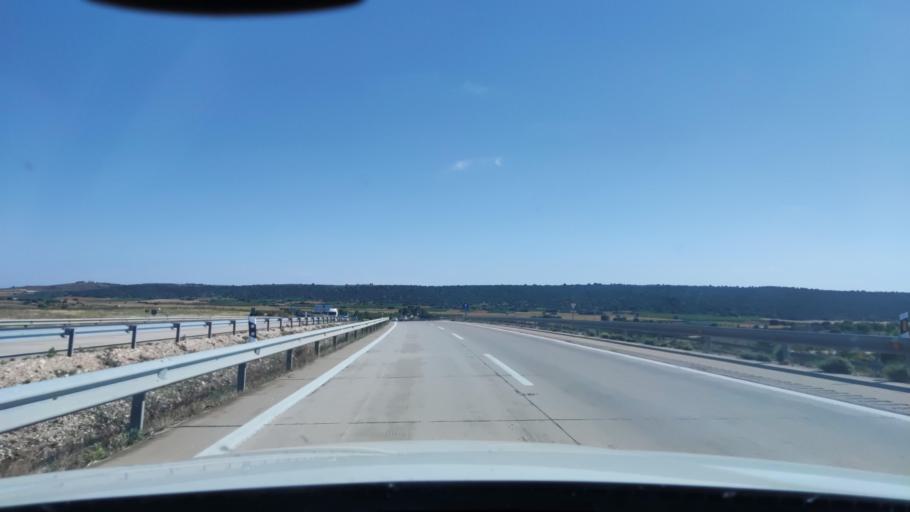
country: ES
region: Castille-La Mancha
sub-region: Provincia de Cuenca
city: Sisante
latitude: 39.4085
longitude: -2.2157
